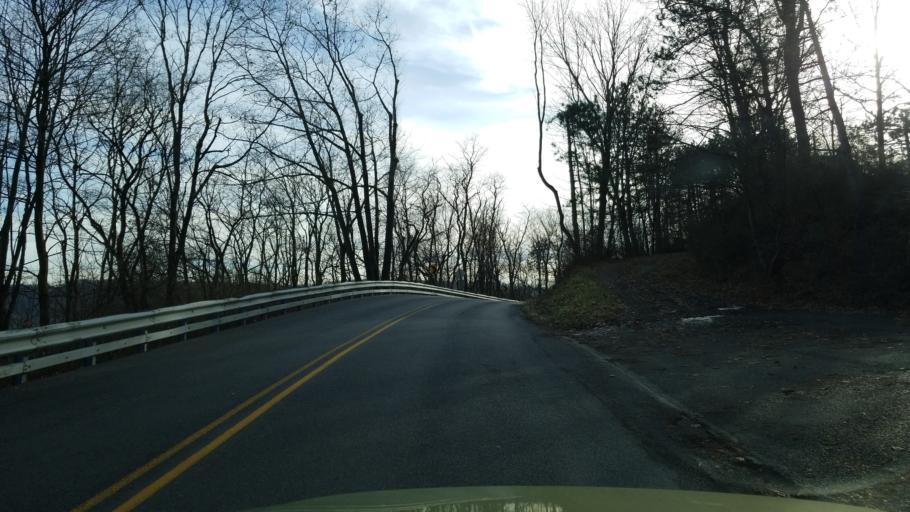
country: US
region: Pennsylvania
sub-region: Clearfield County
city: Clearfield
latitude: 41.0169
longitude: -78.4461
